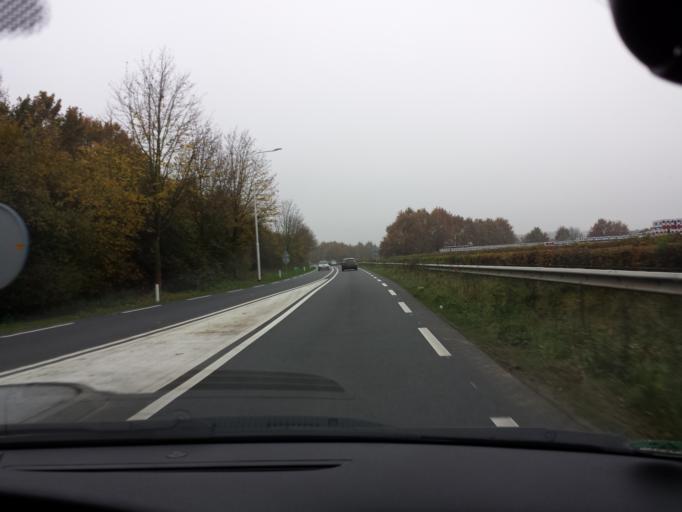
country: NL
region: Limburg
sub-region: Gemeente Sittard-Geleen
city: Born
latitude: 51.0675
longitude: 5.8477
